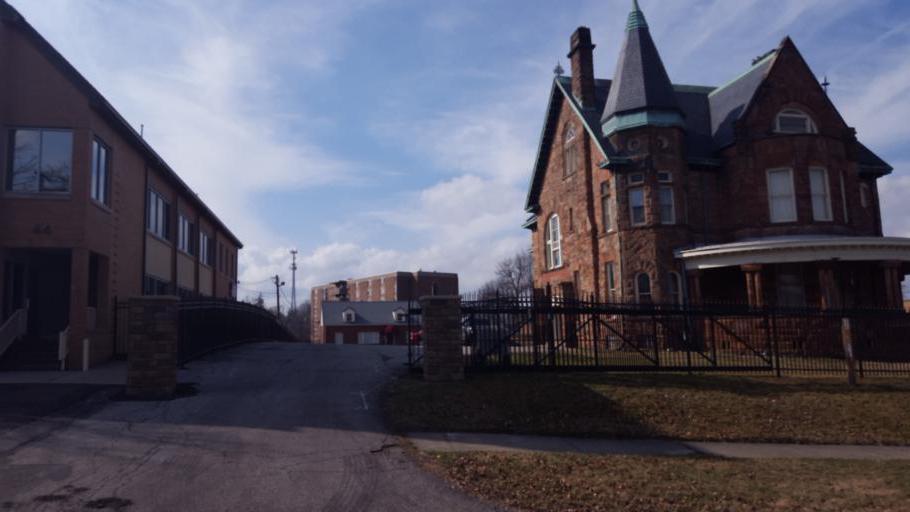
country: US
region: Ohio
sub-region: Richland County
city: Mansfield
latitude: 40.7577
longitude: -82.5233
